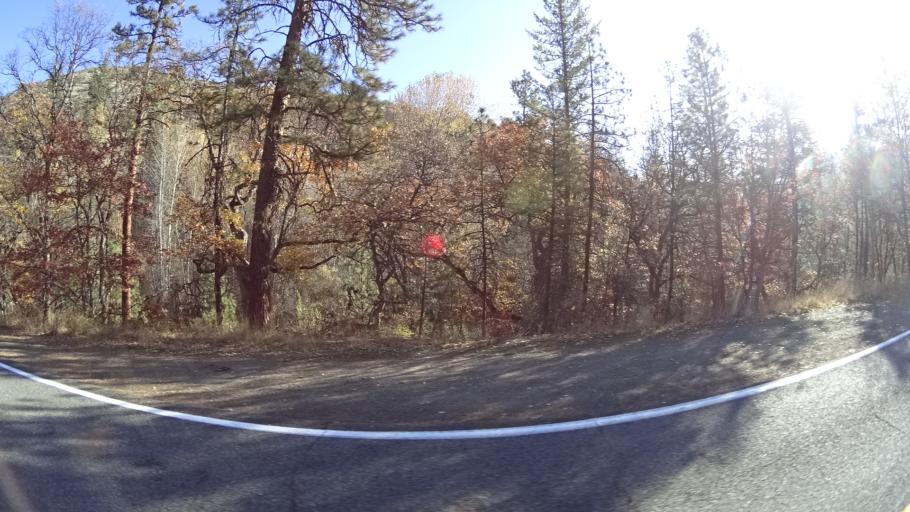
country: US
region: California
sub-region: Siskiyou County
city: Yreka
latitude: 41.8718
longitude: -122.8180
